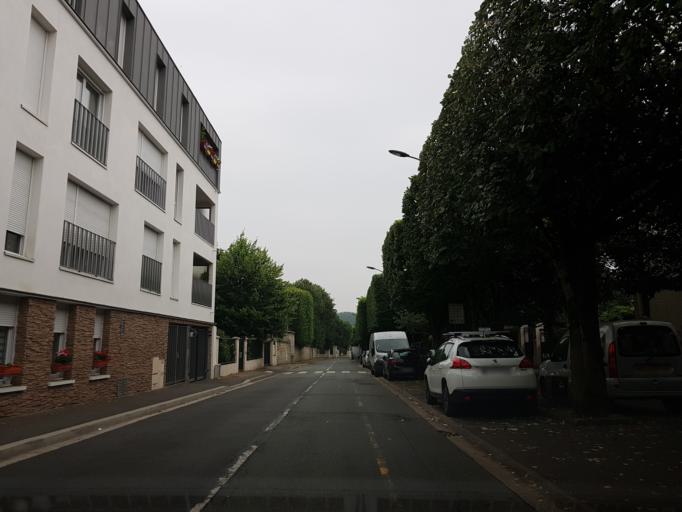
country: FR
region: Ile-de-France
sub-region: Departement des Hauts-de-Seine
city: Bourg-la-Reine
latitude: 48.7784
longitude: 2.3197
